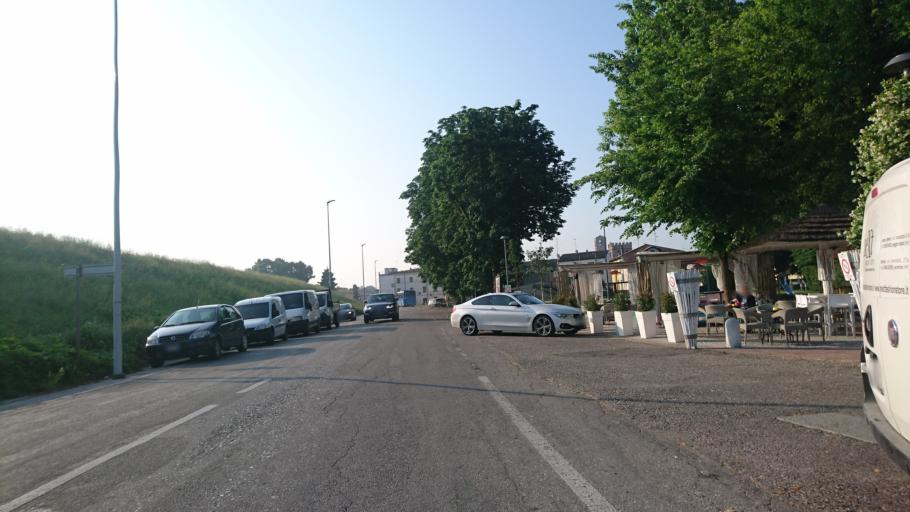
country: IT
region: Lombardy
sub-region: Provincia di Mantova
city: Sermide
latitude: 45.0088
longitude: 11.2979
